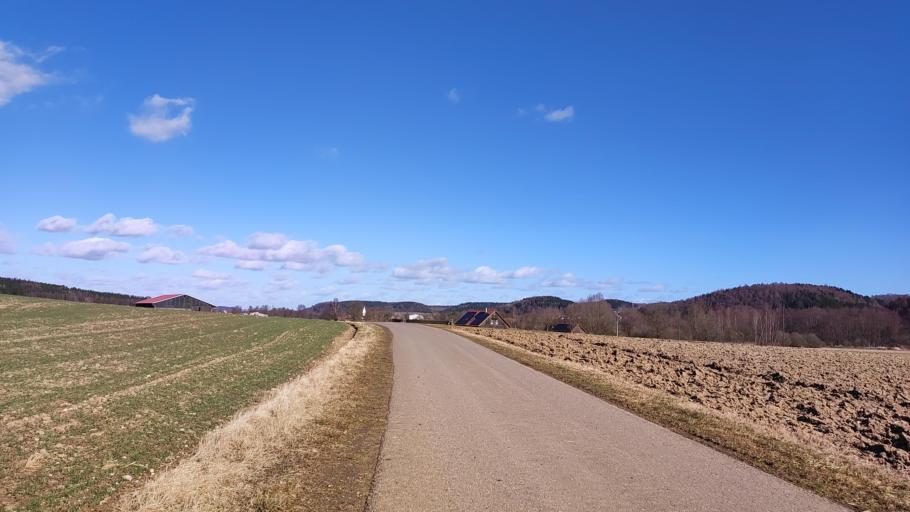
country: DE
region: Bavaria
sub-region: Swabia
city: Zusmarshausen
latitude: 48.4220
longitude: 10.5912
